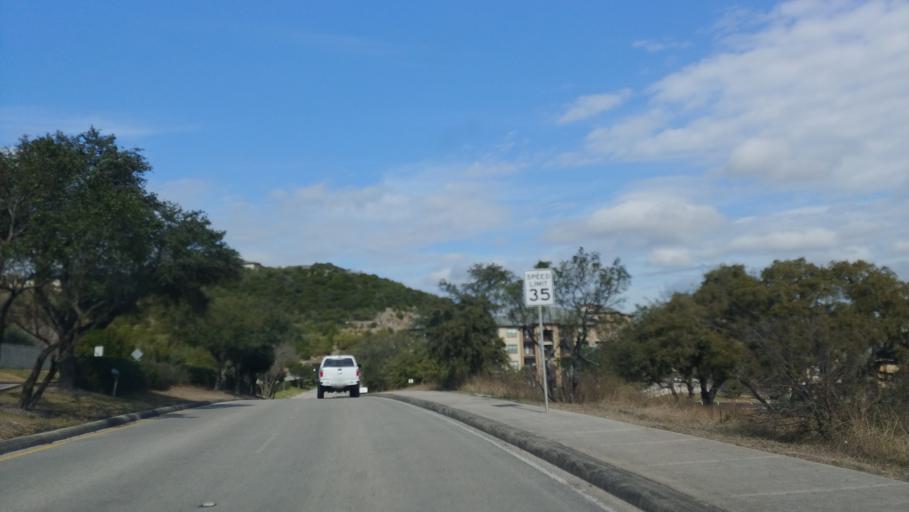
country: US
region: Texas
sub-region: Bexar County
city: Cross Mountain
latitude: 29.6201
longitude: -98.6114
